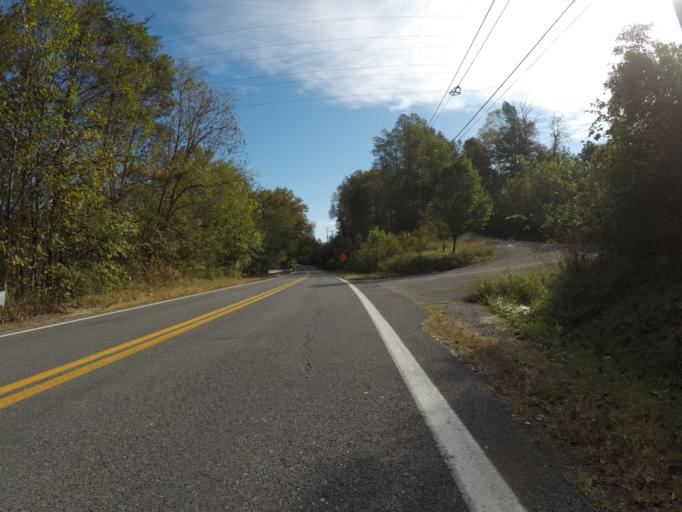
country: US
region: Ohio
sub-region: Lawrence County
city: Burlington
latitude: 38.3563
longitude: -82.5221
